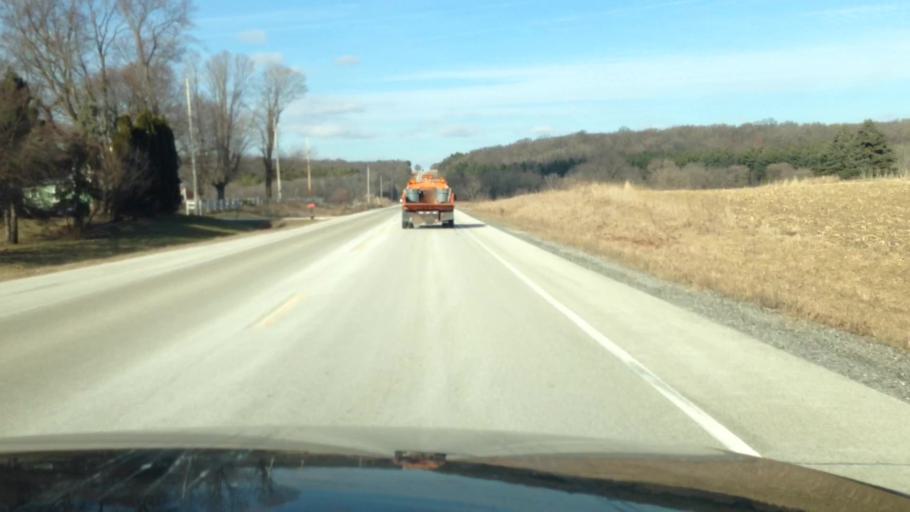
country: US
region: Wisconsin
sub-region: Walworth County
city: East Troy
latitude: 42.7275
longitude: -88.4057
